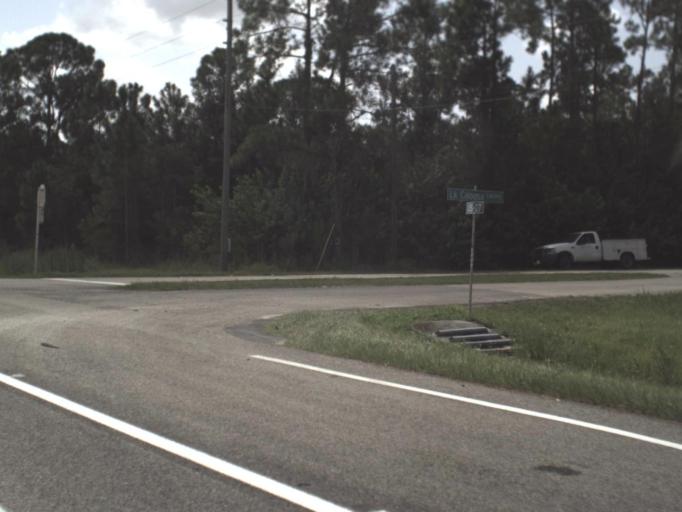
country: US
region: Florida
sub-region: Polk County
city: Crooked Lake Park
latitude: 27.7646
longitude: -81.5945
